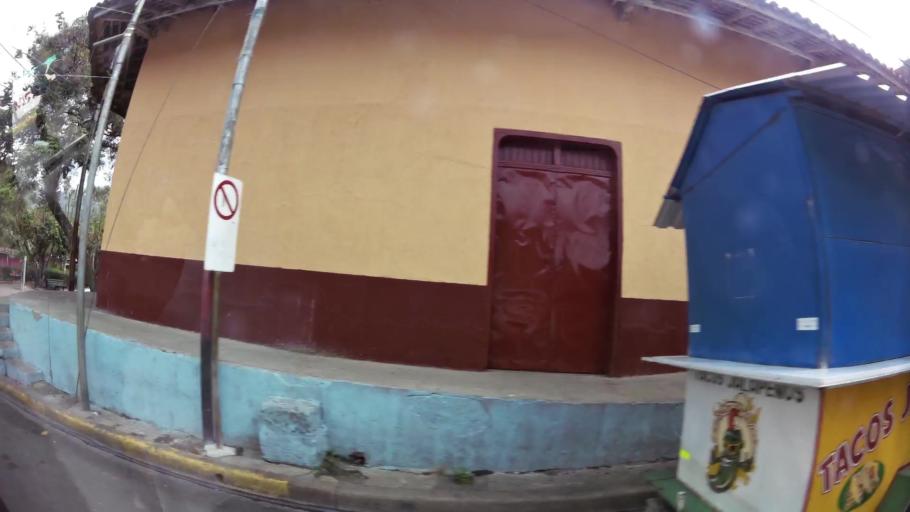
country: NI
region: Matagalpa
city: Matagalpa
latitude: 12.9213
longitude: -85.9195
